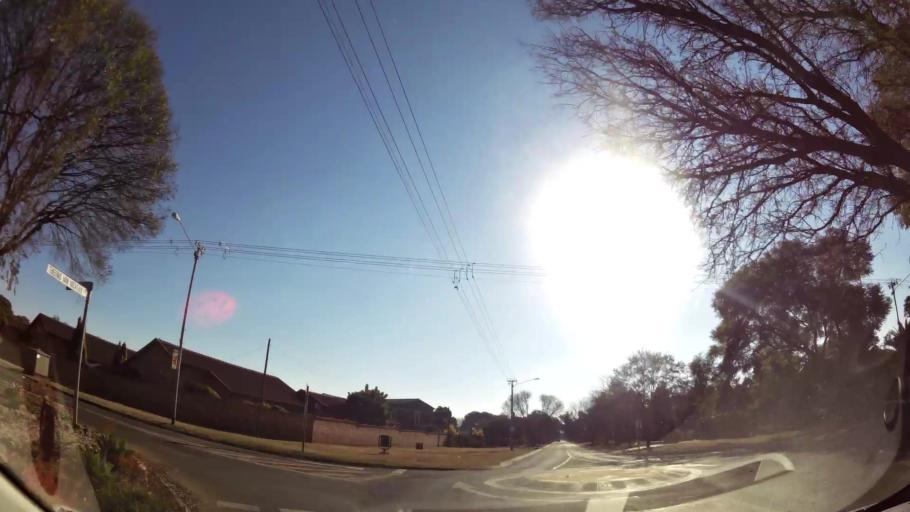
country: ZA
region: Gauteng
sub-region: City of Tshwane Metropolitan Municipality
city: Centurion
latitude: -25.8653
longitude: 28.1472
